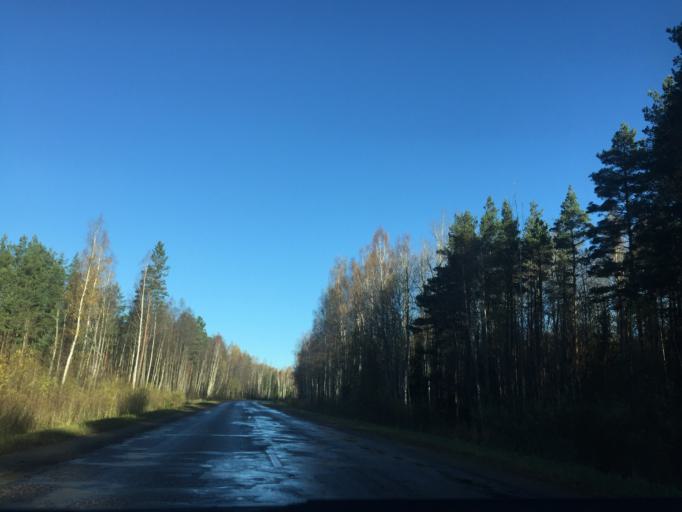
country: LV
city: Tireli
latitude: 56.9158
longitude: 23.5250
